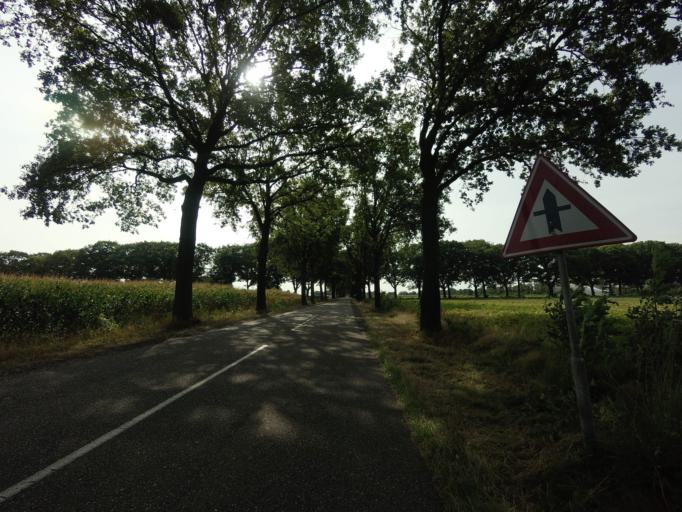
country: NL
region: North Brabant
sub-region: Gemeente Sint Anthonis
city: Sint Anthonis
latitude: 51.5929
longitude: 5.8426
